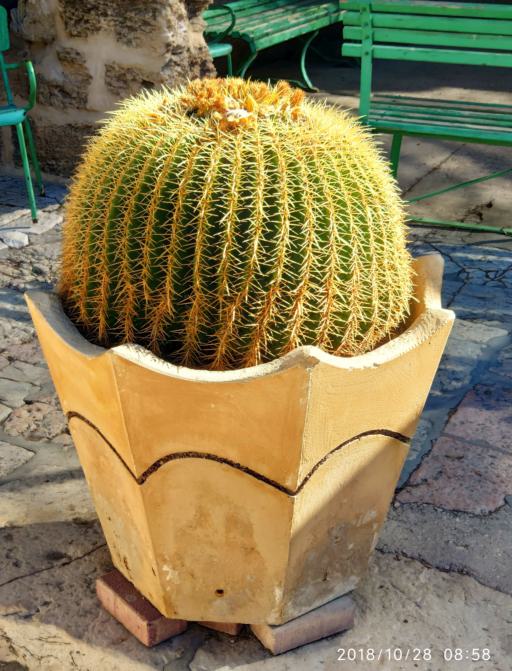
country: PS
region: West Bank
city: Old City
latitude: 31.7781
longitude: 35.2418
